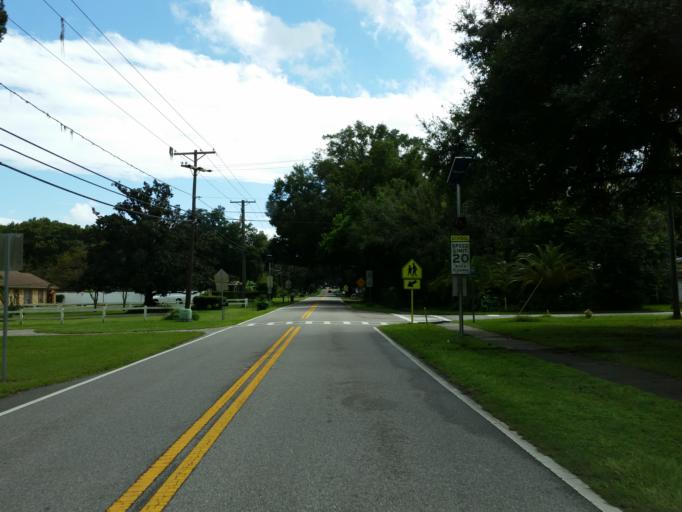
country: US
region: Florida
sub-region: Hillsborough County
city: Brandon
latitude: 27.9154
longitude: -82.2693
